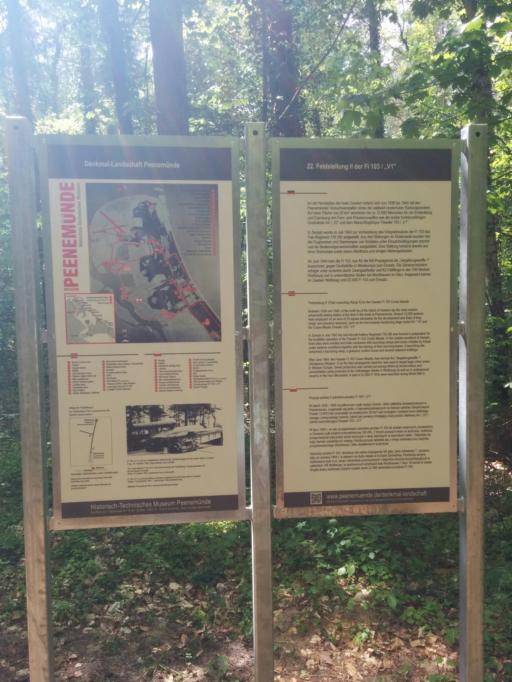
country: DE
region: Mecklenburg-Vorpommern
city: Ostseebad Zinnowitz
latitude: 54.0730
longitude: 13.9305
